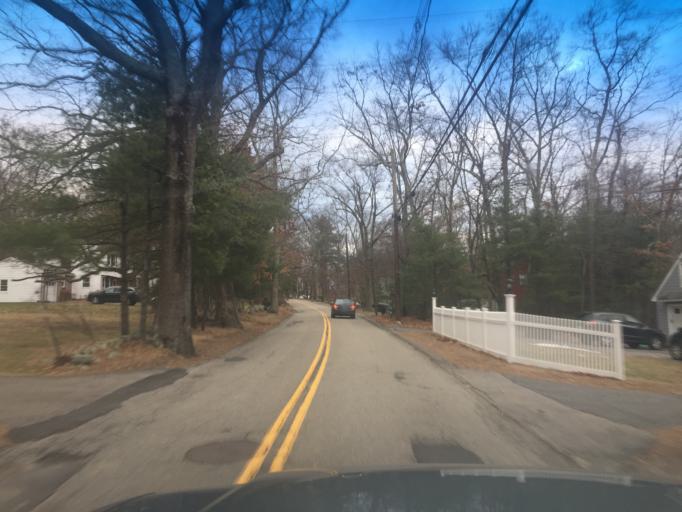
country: US
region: Massachusetts
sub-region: Norfolk County
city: Medway
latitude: 42.1447
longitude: -71.3808
